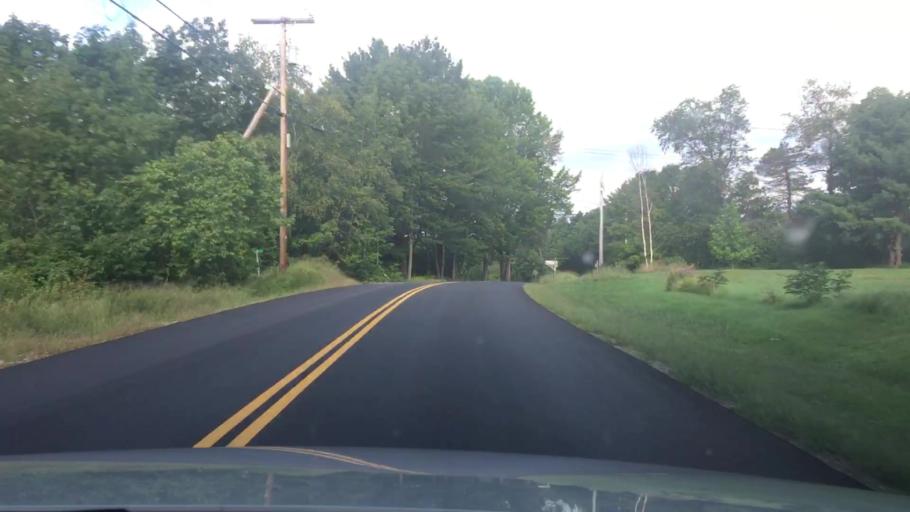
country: US
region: Maine
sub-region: Androscoggin County
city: Lisbon Falls
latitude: 44.0415
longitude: -70.0408
